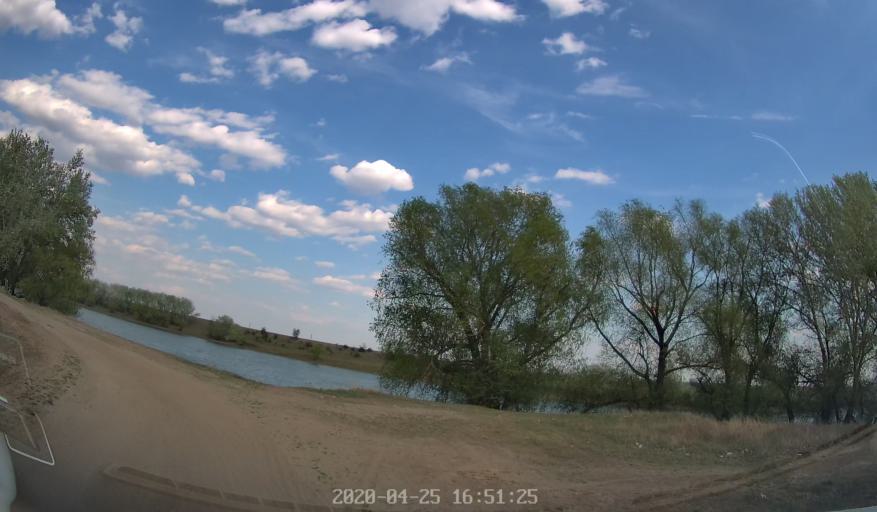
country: MD
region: Chisinau
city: Vadul lui Voda
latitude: 47.1273
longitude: 29.0858
